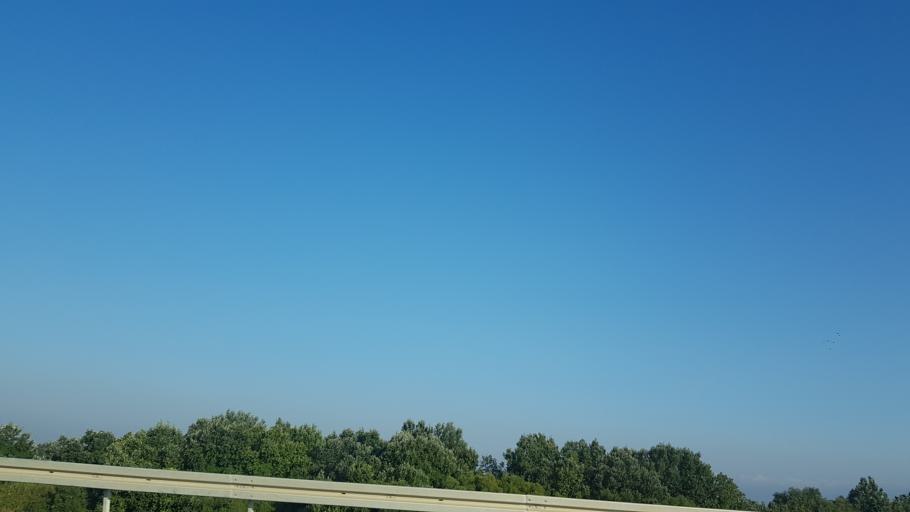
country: TR
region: Bursa
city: Karacabey
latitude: 40.1816
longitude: 28.3304
